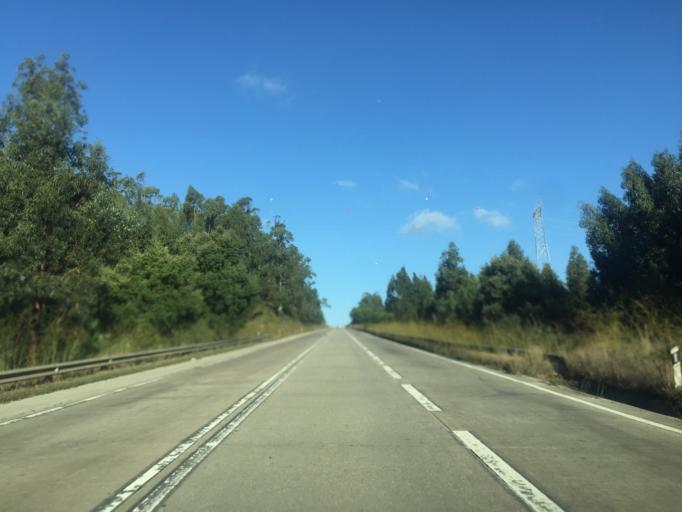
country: PT
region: Santarem
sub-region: Rio Maior
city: Rio Maior
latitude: 39.3389
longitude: -8.9666
